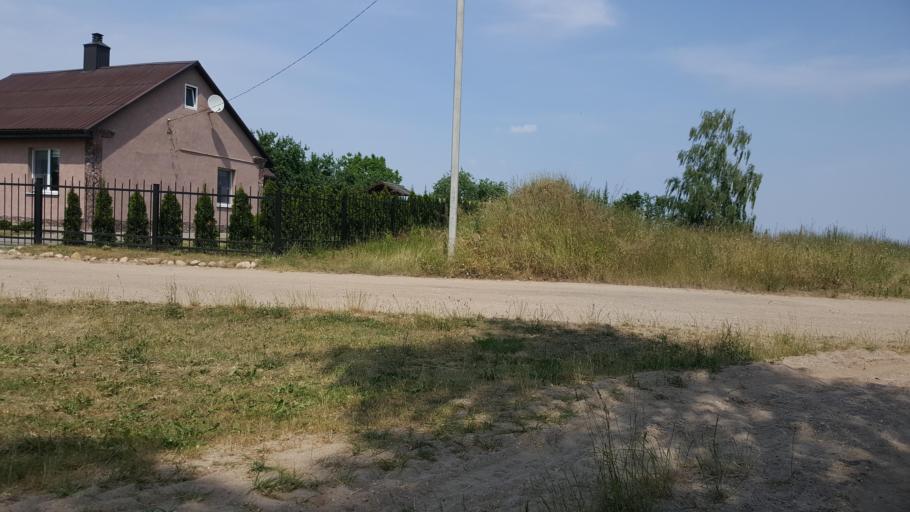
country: BY
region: Brest
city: Kamyanyets
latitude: 52.3717
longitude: 23.7876
